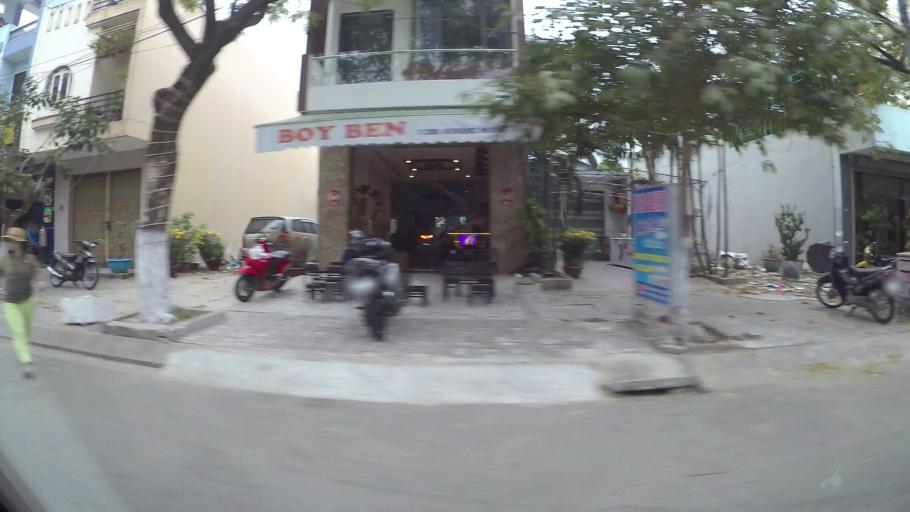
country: VN
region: Da Nang
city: Da Nang
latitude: 16.0908
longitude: 108.2348
